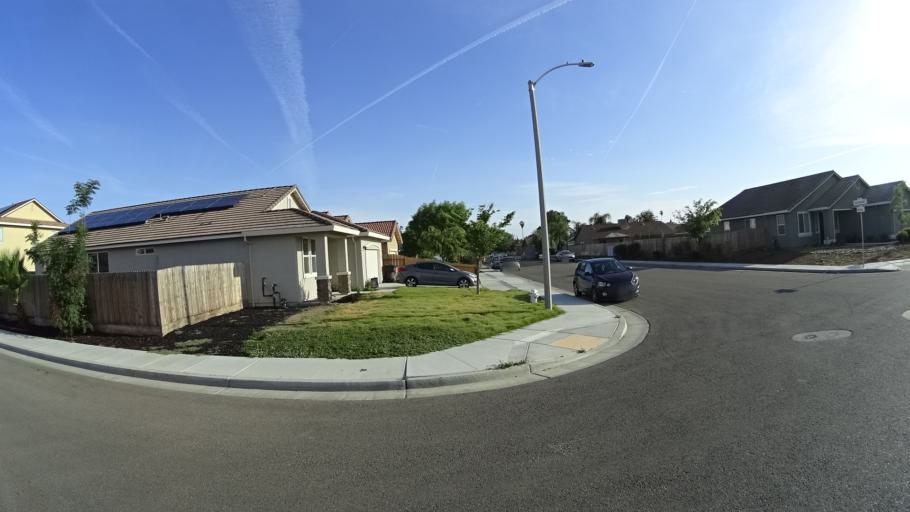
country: US
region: California
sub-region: Kings County
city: Armona
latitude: 36.3079
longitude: -119.6772
